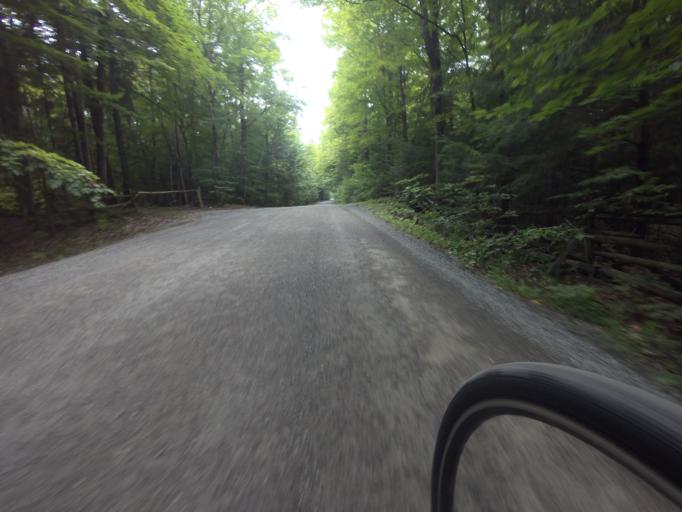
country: CA
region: Ontario
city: Carleton Place
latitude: 45.2349
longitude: -76.2856
